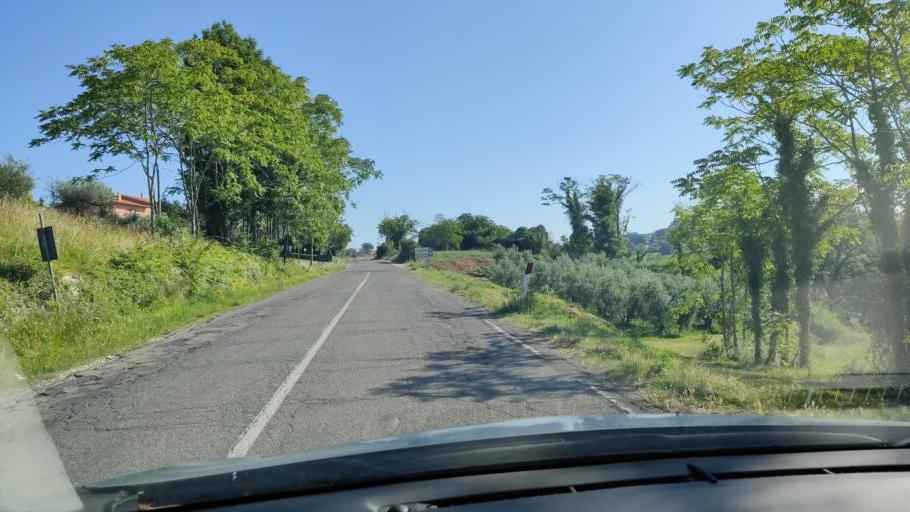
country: IT
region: Umbria
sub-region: Provincia di Terni
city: Avigliano Umbro
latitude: 42.6475
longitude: 12.4190
